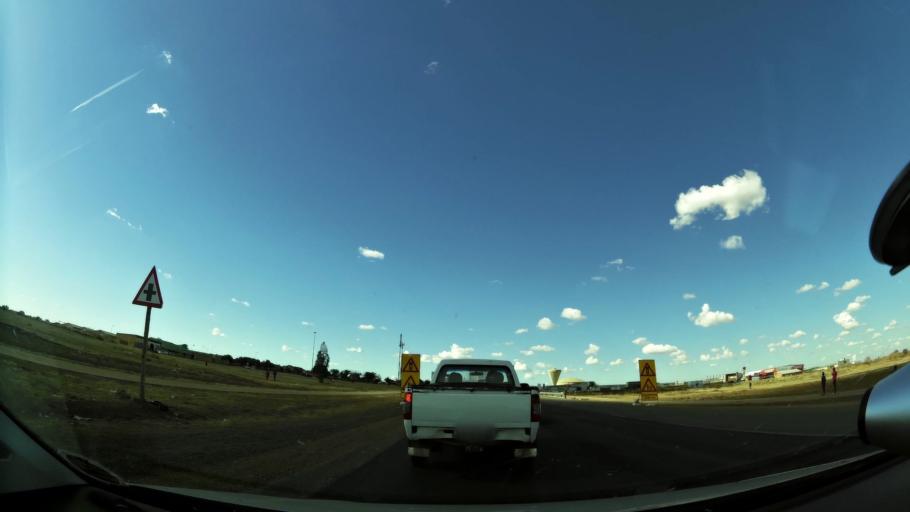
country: ZA
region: North-West
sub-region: Dr Kenneth Kaunda District Municipality
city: Klerksdorp
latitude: -26.8767
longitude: 26.5877
